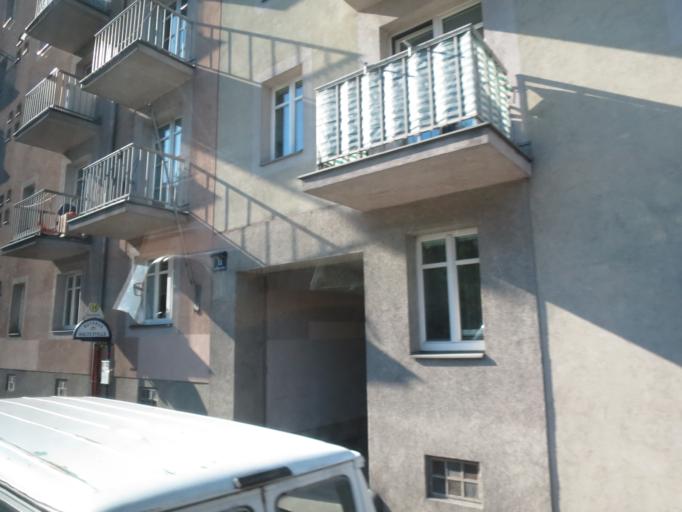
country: AT
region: Vienna
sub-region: Wien Stadt
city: Vienna
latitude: 48.1839
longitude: 16.3457
